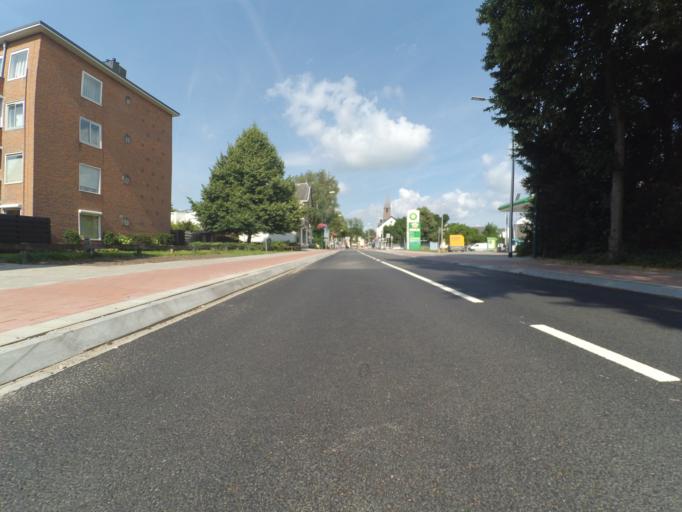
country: NL
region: Utrecht
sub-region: Gemeente Utrechtse Heuvelrug
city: Driebergen-Rijsenburg
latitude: 52.0513
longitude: 5.2842
